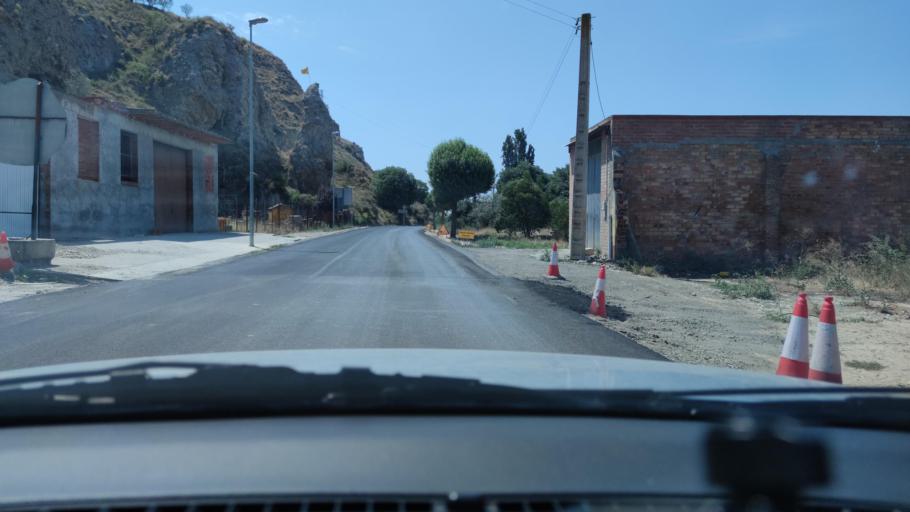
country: ES
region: Catalonia
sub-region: Provincia de Lleida
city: Alfarras
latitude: 41.8475
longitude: 0.5852
